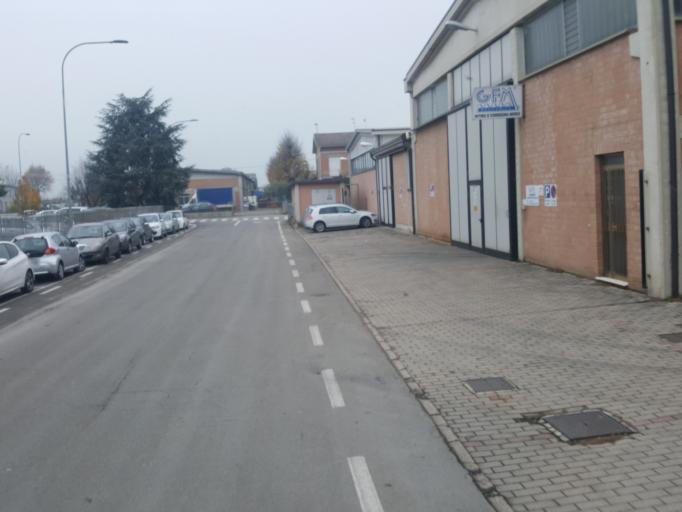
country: IT
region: Emilia-Romagna
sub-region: Provincia di Reggio Emilia
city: Codemondo-Quaresimo
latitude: 44.7178
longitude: 10.5525
